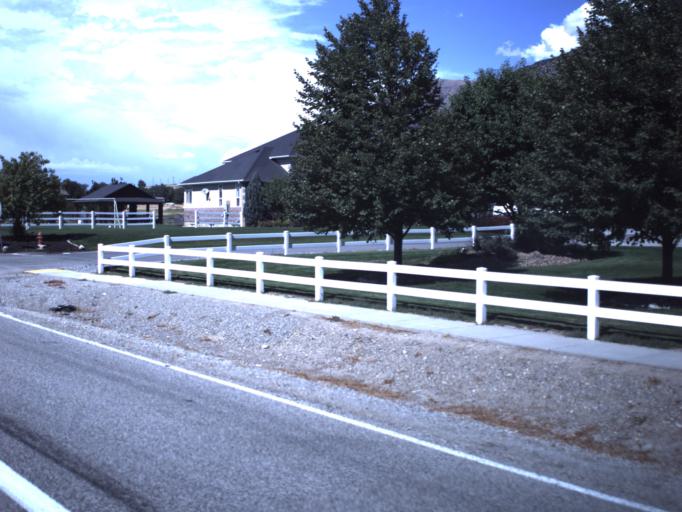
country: US
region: Utah
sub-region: Box Elder County
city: Honeyville
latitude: 41.6146
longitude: -112.0655
